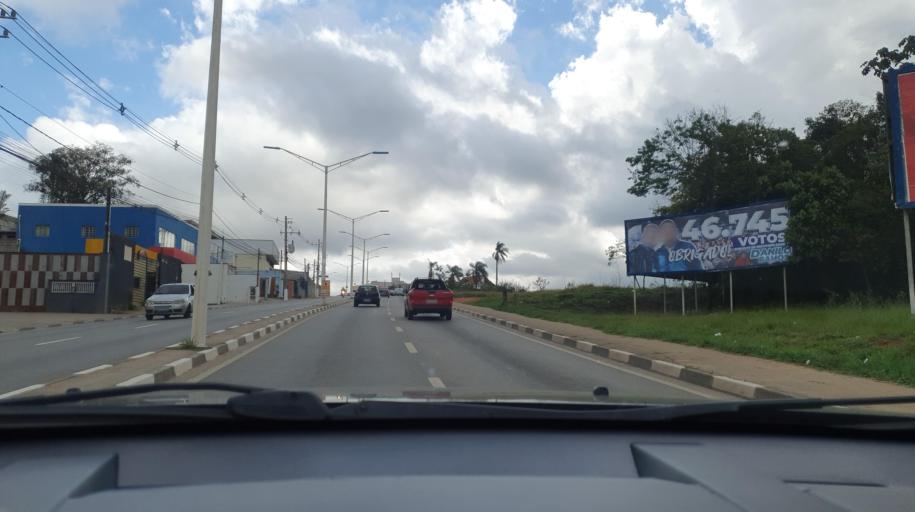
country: BR
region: Sao Paulo
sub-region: Vargem Grande Paulista
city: Vargem Grande Paulista
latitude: -23.6453
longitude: -46.9925
